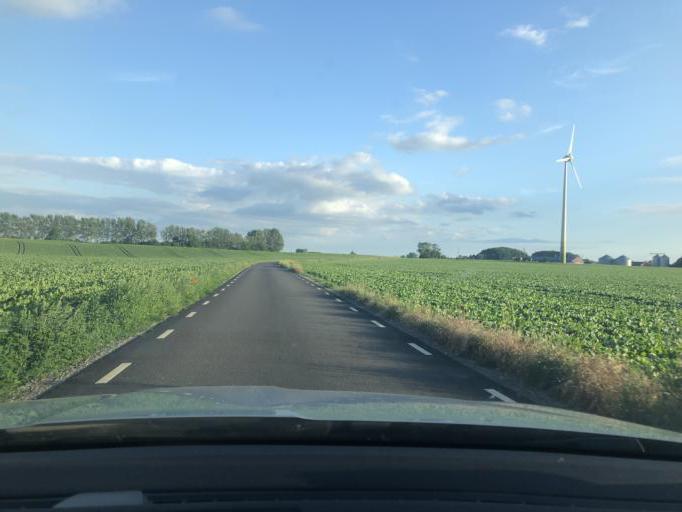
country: SE
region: Skane
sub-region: Simrishamns Kommun
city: Simrishamn
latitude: 55.4740
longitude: 14.1935
